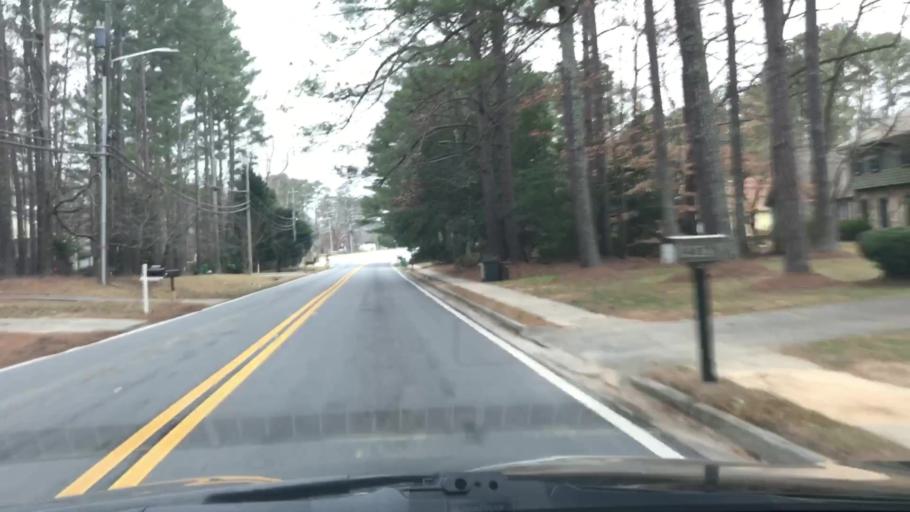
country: US
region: Georgia
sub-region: DeKalb County
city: Doraville
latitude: 33.9365
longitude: -84.2908
